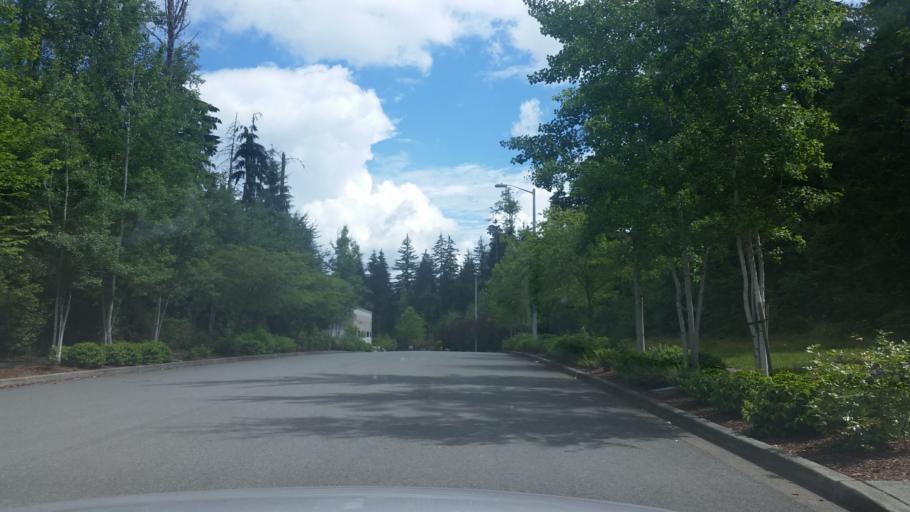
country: US
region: Washington
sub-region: King County
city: Union Hill-Novelty Hill
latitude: 47.6899
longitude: -122.0331
